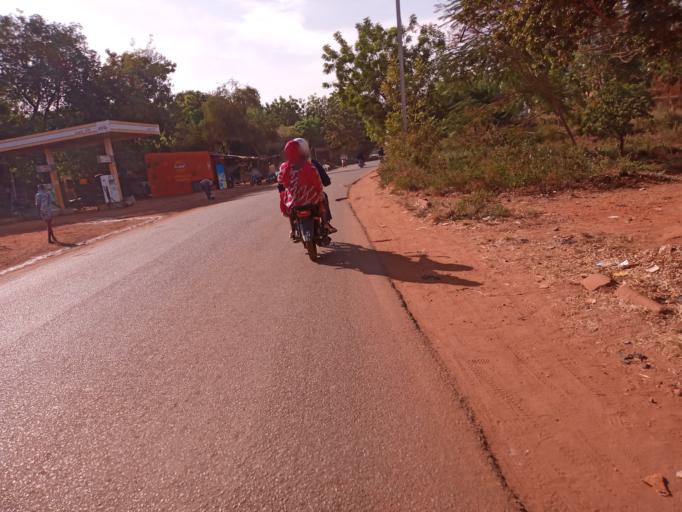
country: ML
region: Bamako
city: Bamako
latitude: 12.6291
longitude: -7.9495
